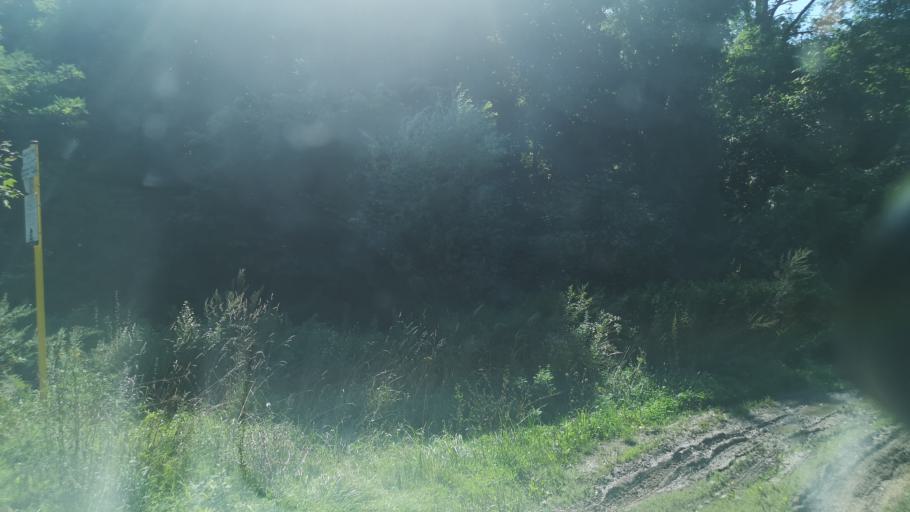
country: SK
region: Trnavsky
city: Smolenice
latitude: 48.5825
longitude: 17.4300
